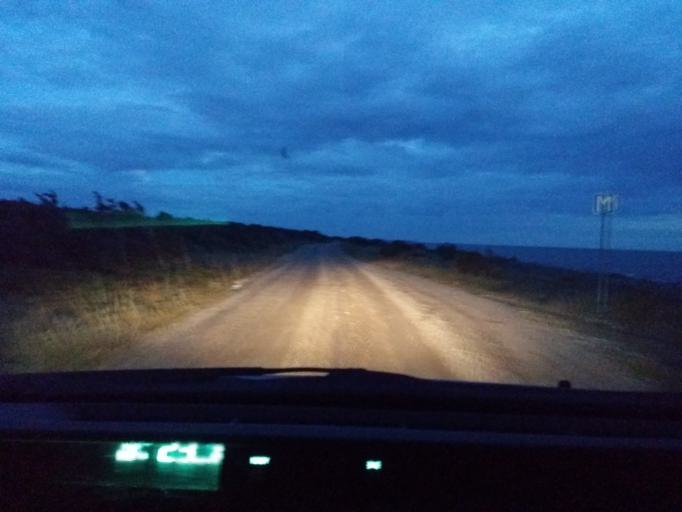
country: SE
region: Kalmar
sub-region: Borgholms Kommun
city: Borgholm
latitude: 57.1420
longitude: 16.9073
